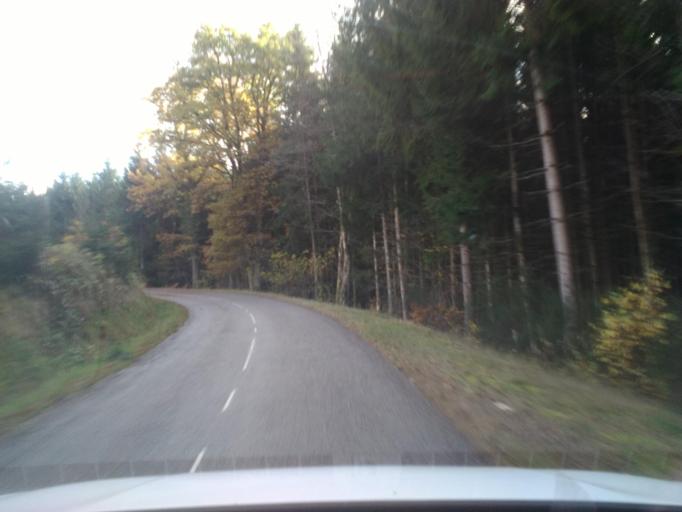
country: FR
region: Lorraine
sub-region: Departement des Vosges
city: Senones
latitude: 48.3680
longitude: 7.0243
